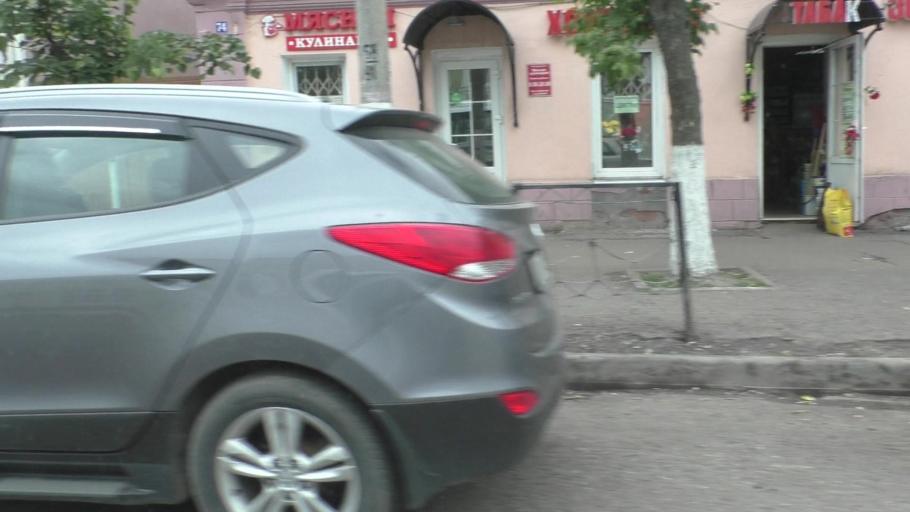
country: RU
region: Moskovskaya
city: Yegor'yevsk
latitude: 55.3842
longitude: 39.0339
